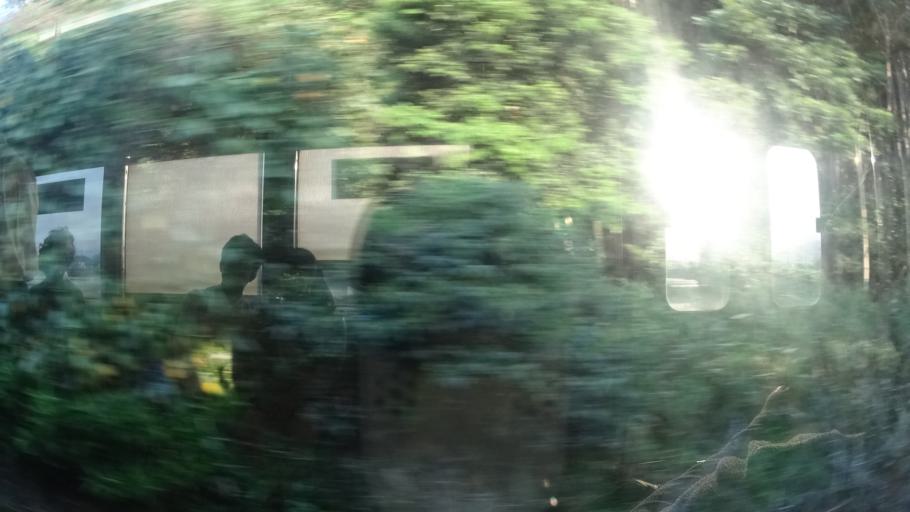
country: JP
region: Aichi
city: Tahara
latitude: 34.6848
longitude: 137.3240
